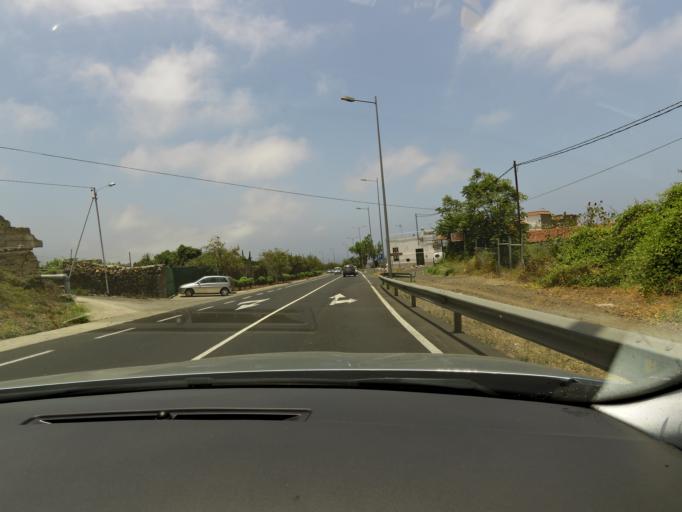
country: ES
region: Canary Islands
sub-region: Provincia de Santa Cruz de Tenerife
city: La Orotava
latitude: 28.4048
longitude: -16.5222
